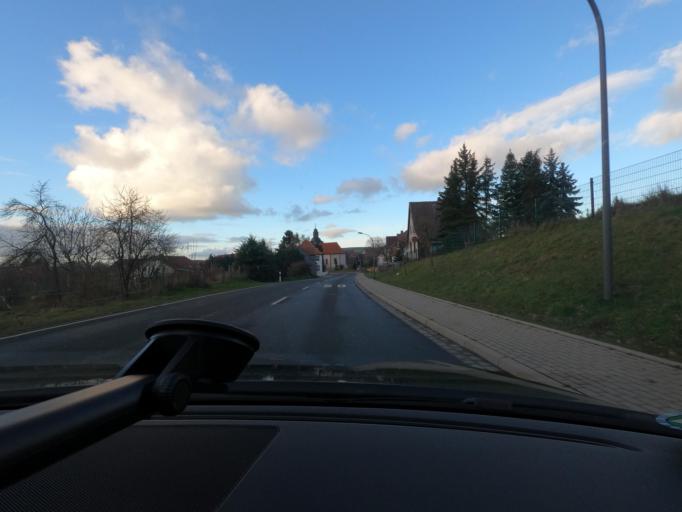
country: DE
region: Thuringia
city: Ferna
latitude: 51.4555
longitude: 10.3108
